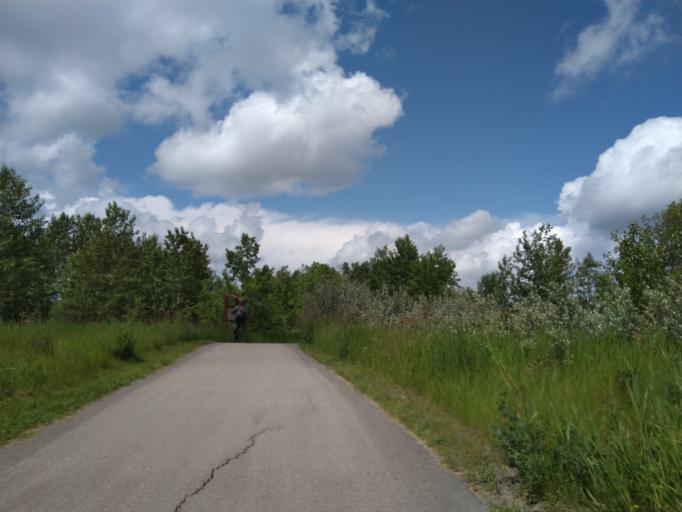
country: CA
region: Alberta
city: Cochrane
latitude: 51.1868
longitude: -114.4940
